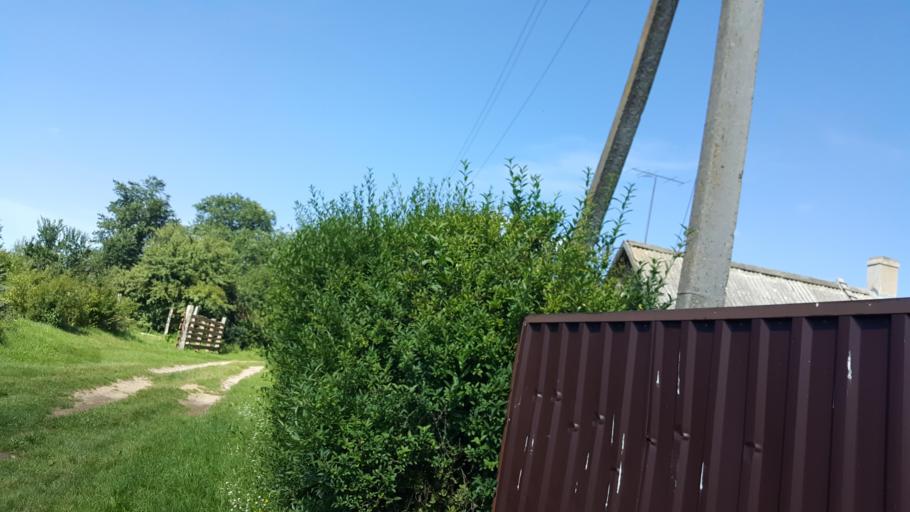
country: BY
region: Brest
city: Charnawchytsy
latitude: 52.3551
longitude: 23.6204
